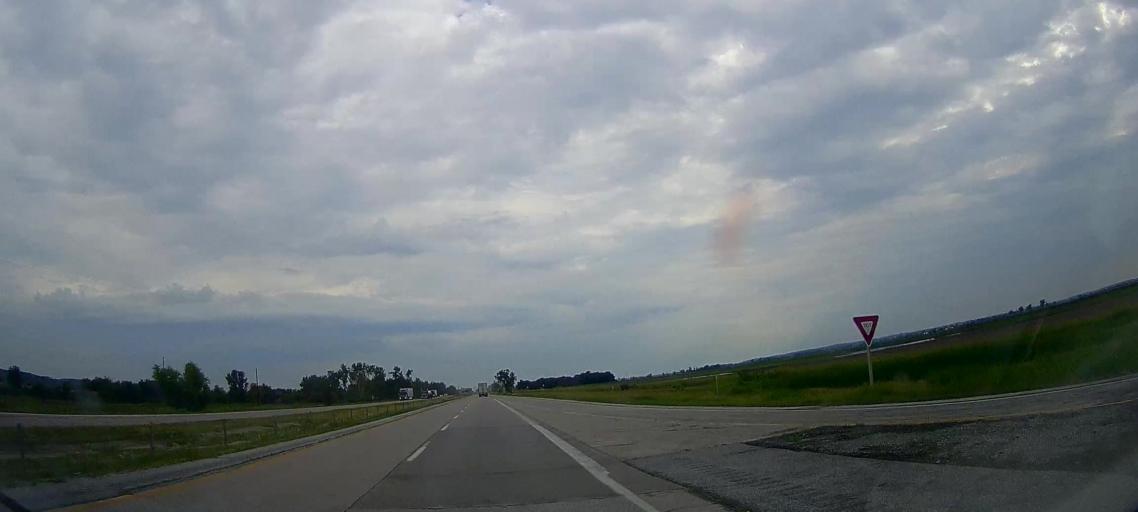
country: US
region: Iowa
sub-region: Harrison County
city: Missouri Valley
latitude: 41.4872
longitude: -95.9008
